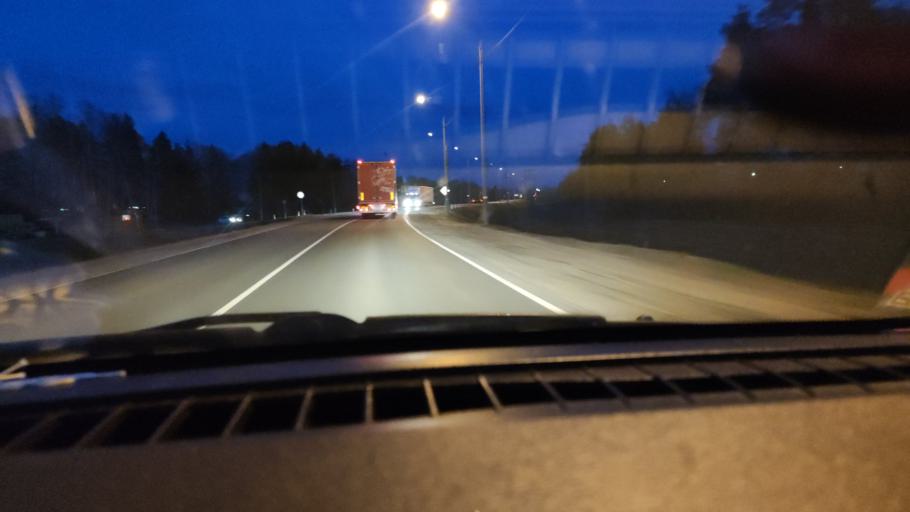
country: RU
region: Saratov
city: Sennoy
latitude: 52.1514
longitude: 46.9704
